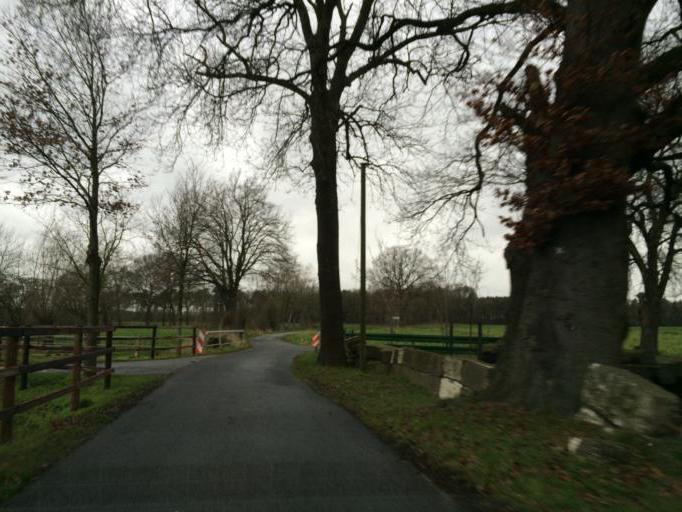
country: DE
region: North Rhine-Westphalia
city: Marl
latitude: 51.7036
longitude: 7.0725
